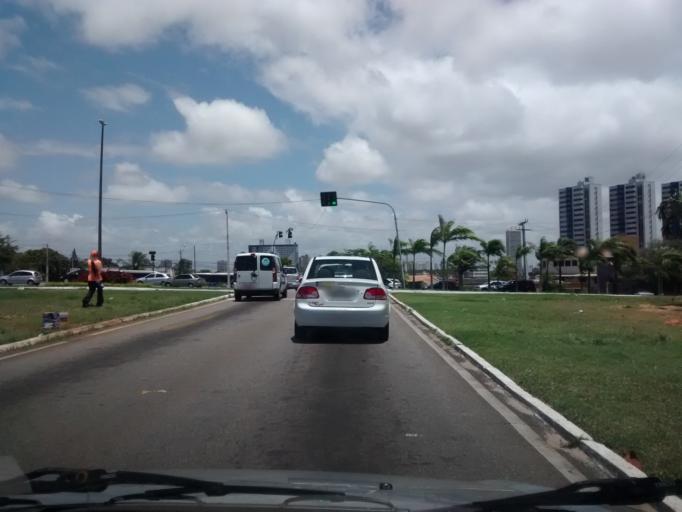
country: BR
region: Rio Grande do Norte
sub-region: Natal
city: Natal
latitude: -5.8670
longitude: -35.1824
